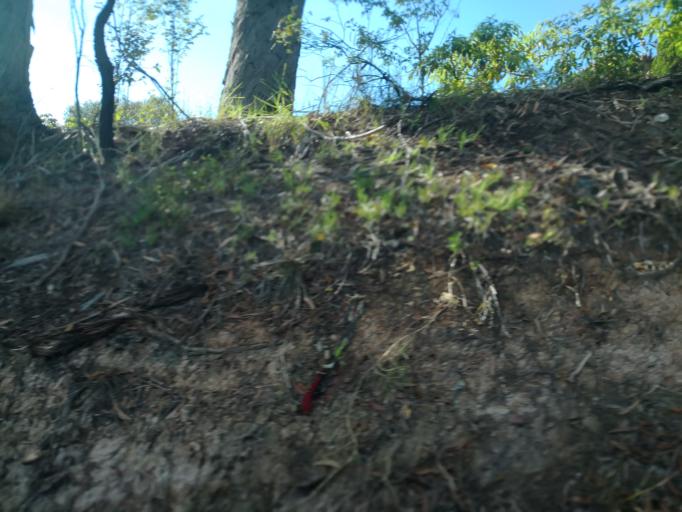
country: AU
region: New South Wales
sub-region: Gosford Shire
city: Gosford
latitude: -33.4136
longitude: 151.3446
